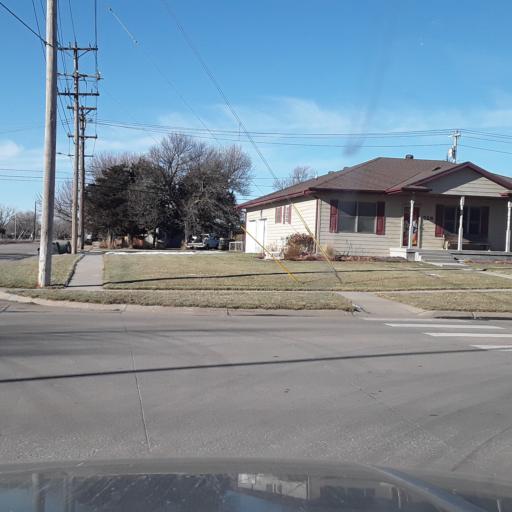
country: US
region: Nebraska
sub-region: Adams County
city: Hastings
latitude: 40.5771
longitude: -98.4018
